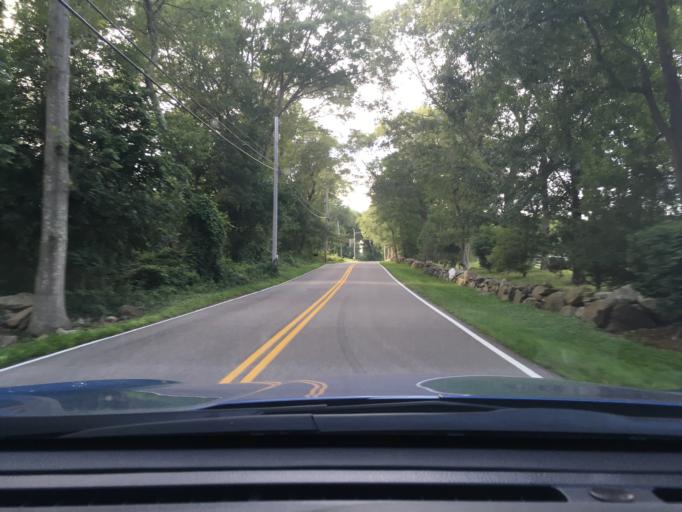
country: US
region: Rhode Island
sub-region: Washington County
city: Exeter
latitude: 41.6198
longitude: -71.5104
